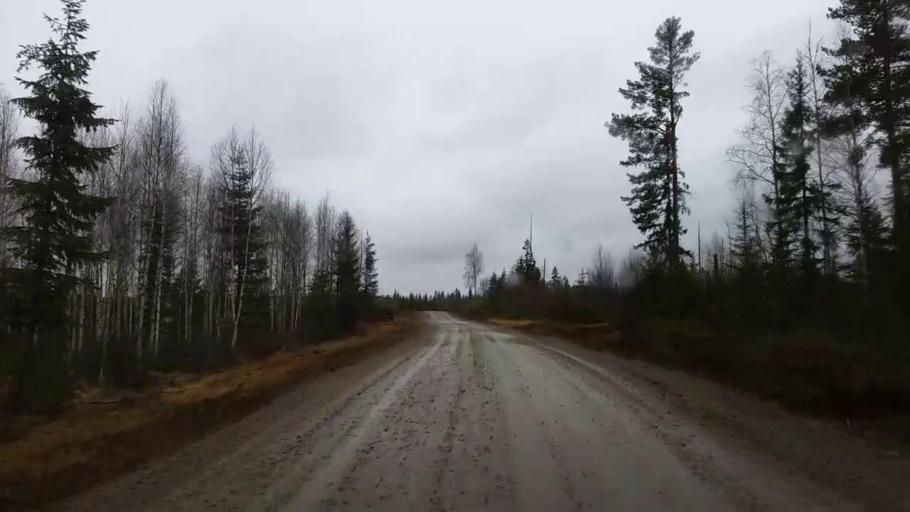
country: SE
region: Gaevleborg
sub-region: Ljusdals Kommun
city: Farila
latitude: 62.1302
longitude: 15.6639
